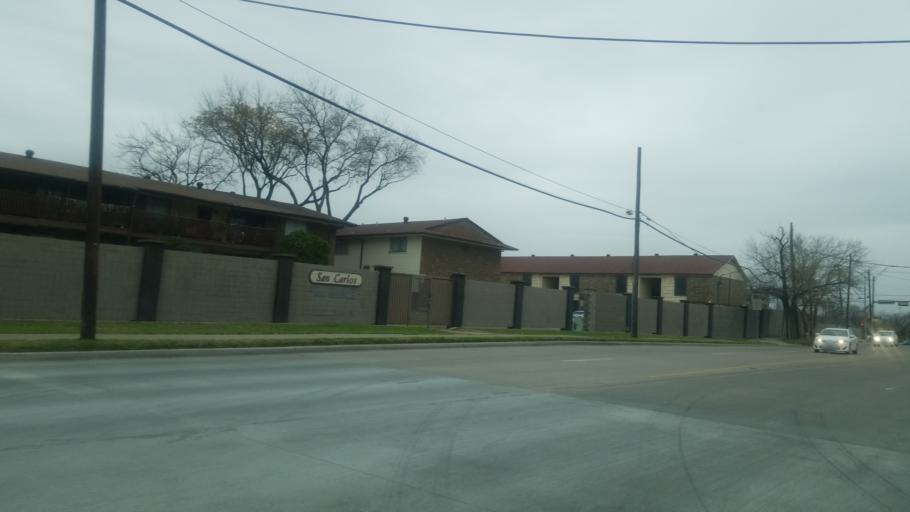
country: US
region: Texas
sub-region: Dallas County
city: Dallas
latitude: 32.8160
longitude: -96.8302
